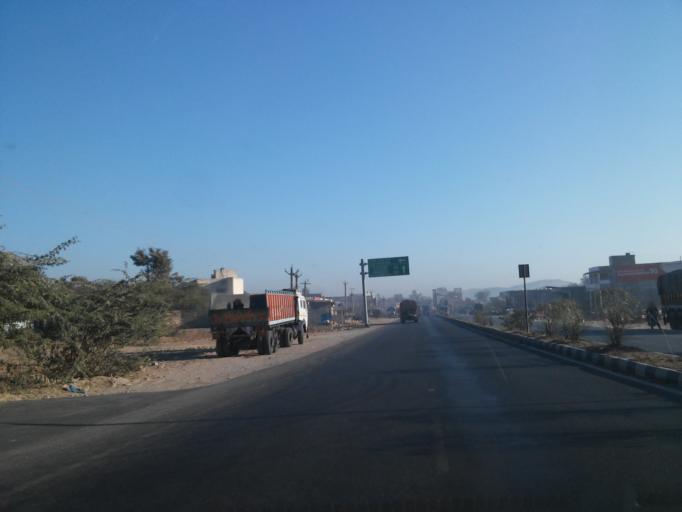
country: IN
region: Rajasthan
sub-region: Dungarpur
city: Dungarpur
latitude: 23.9689
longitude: 73.5865
